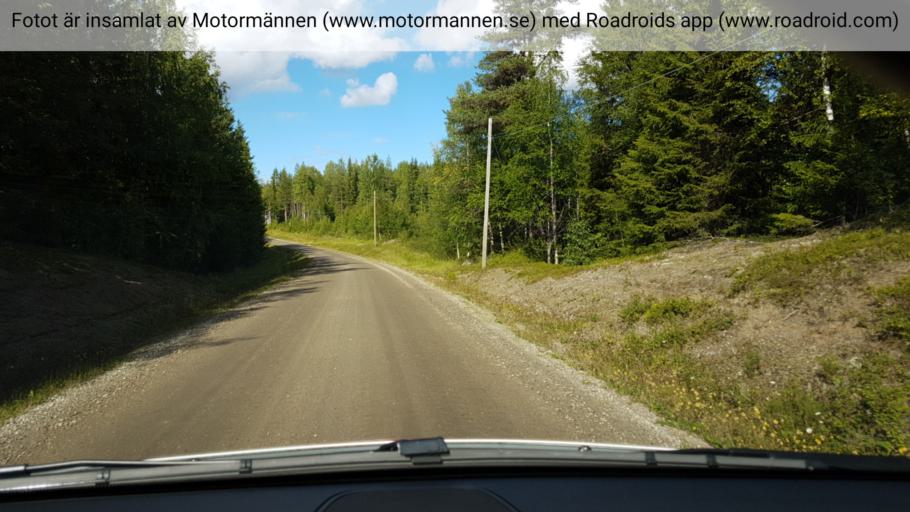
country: SE
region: Jaemtland
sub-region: Ragunda Kommun
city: Hammarstrand
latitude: 63.2965
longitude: 15.9965
